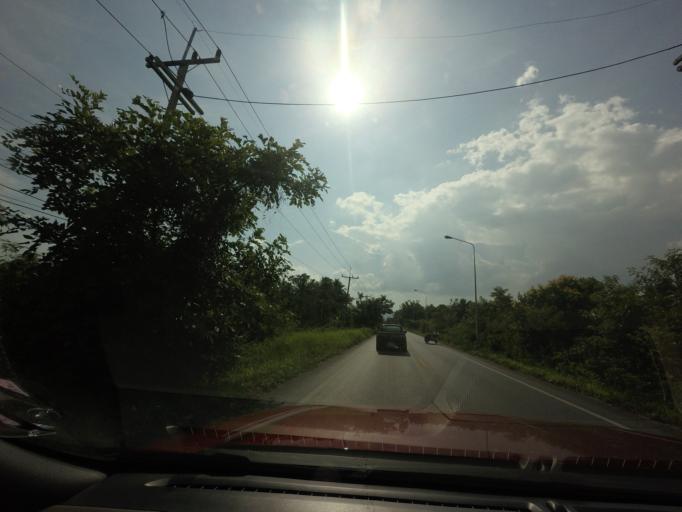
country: TH
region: Yala
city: Yala
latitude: 6.5556
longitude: 101.2246
